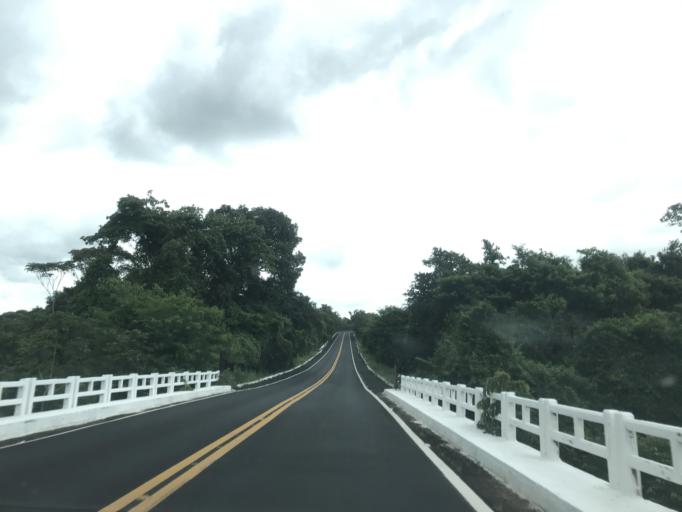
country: BR
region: Goias
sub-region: Caldas Novas
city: Caldas Novas
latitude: -17.7363
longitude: -48.7685
